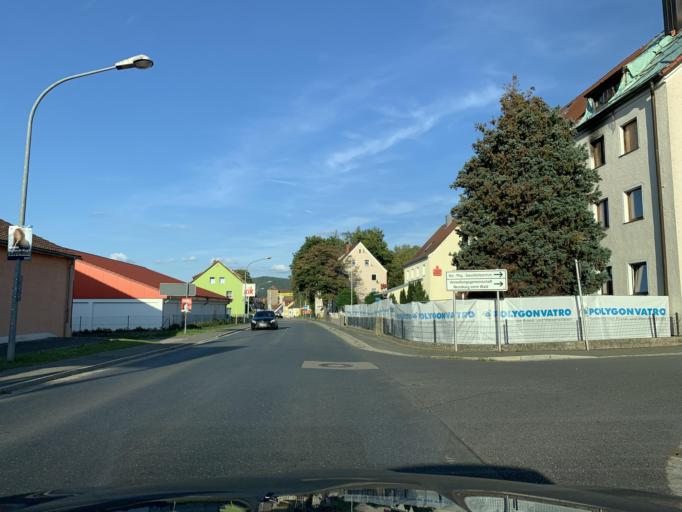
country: DE
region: Bavaria
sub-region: Upper Palatinate
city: Neunburg vorm Wald
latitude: 49.3466
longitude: 12.3770
